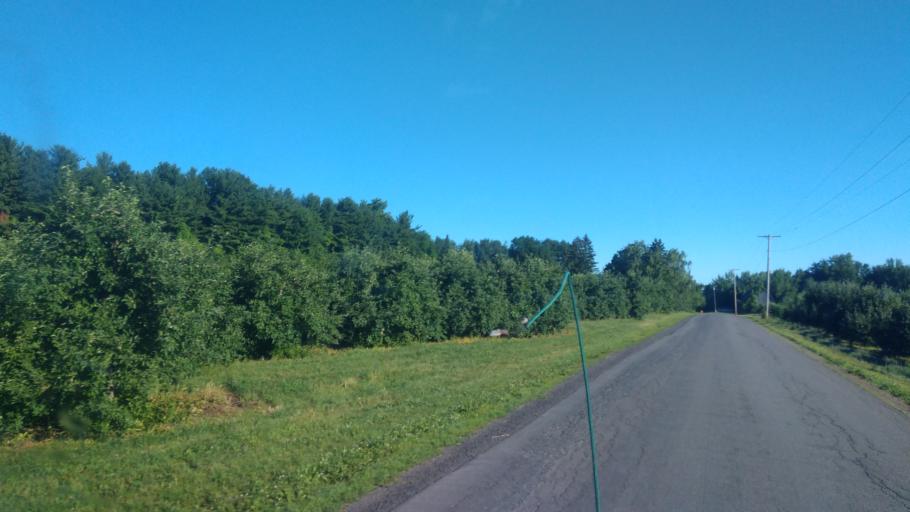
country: US
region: New York
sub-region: Wayne County
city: Sodus
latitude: 43.1861
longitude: -77.0621
